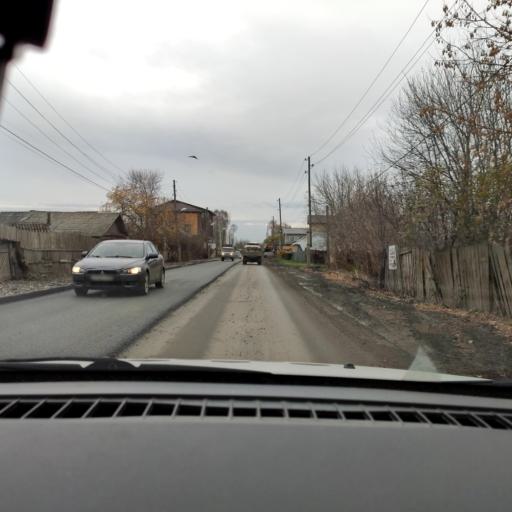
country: RU
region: Perm
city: Kondratovo
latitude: 57.9662
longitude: 56.1190
